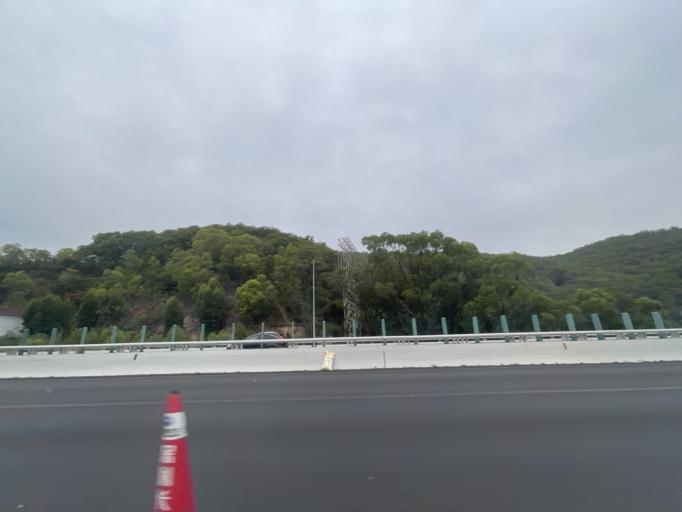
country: CN
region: Guangdong
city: Xinwan
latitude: 22.8013
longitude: 113.6229
